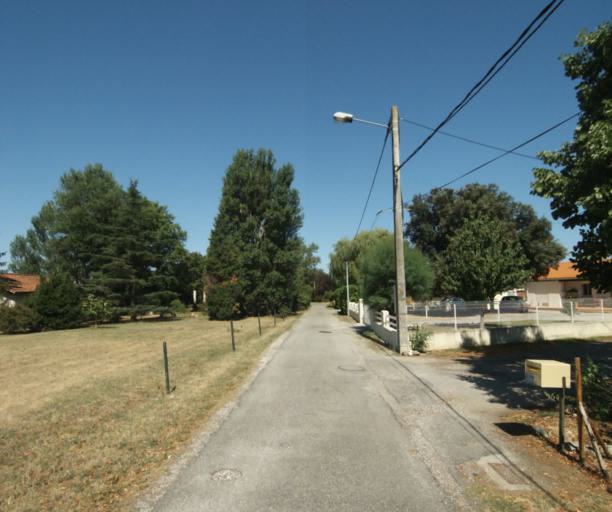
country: FR
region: Midi-Pyrenees
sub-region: Departement de la Haute-Garonne
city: Revel
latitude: 43.4680
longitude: 1.9953
